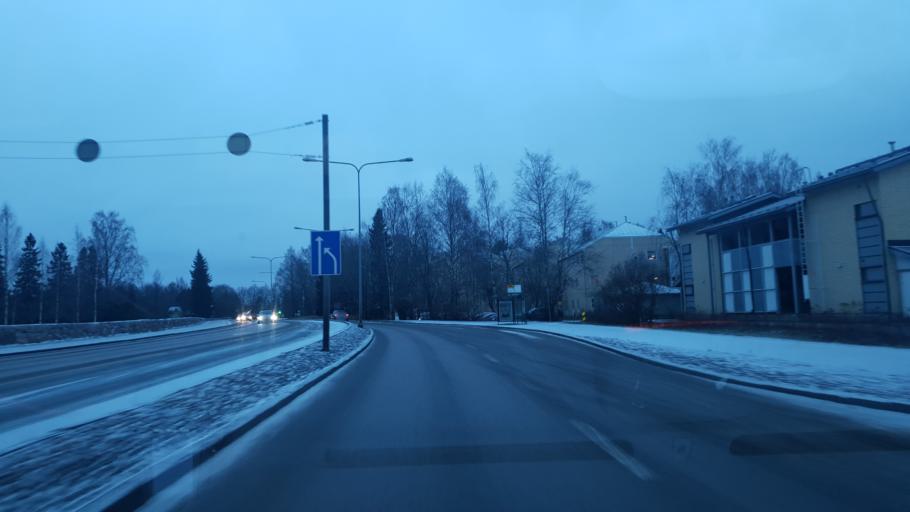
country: FI
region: Uusimaa
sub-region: Helsinki
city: Vantaa
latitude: 60.2391
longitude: 25.0210
